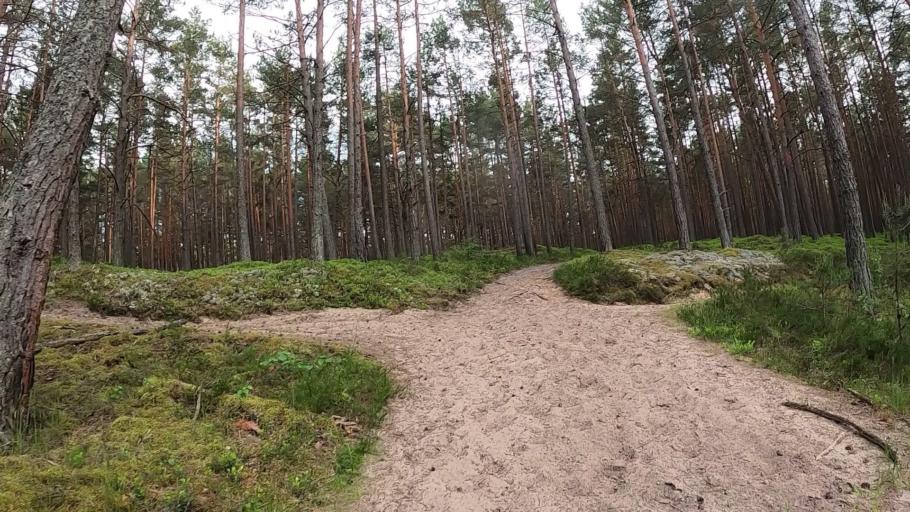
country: LV
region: Riga
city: Jaunciems
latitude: 57.0902
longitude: 24.1631
